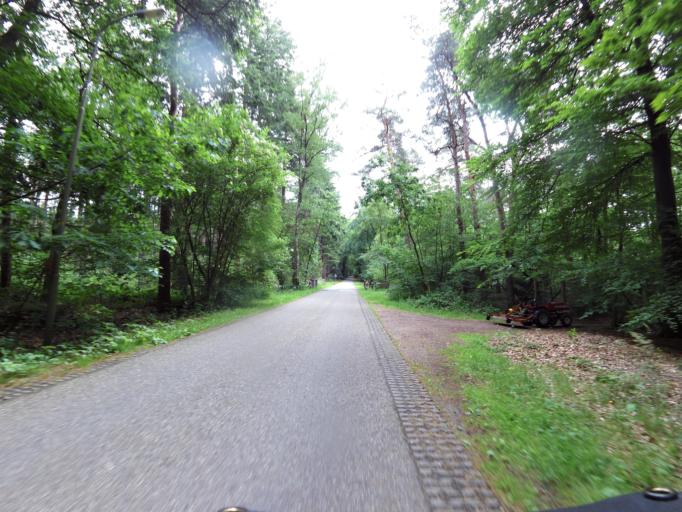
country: NL
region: Gelderland
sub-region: Gemeente Apeldoorn
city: Uddel
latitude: 52.2854
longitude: 5.7978
